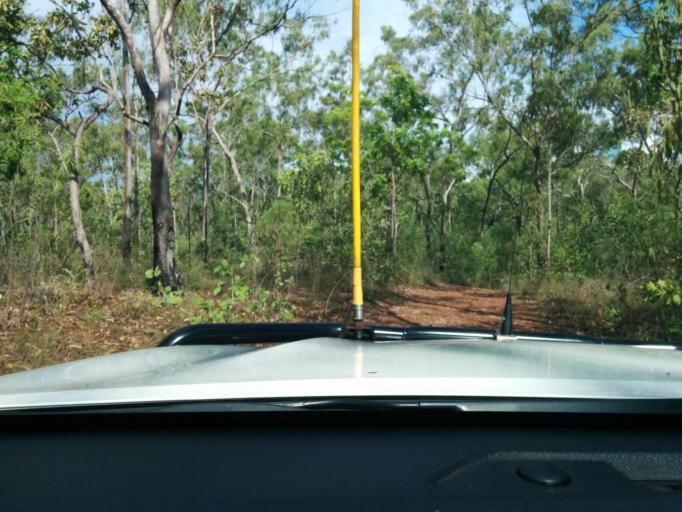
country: AU
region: Northern Territory
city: Alyangula
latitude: -13.8453
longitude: 136.4197
